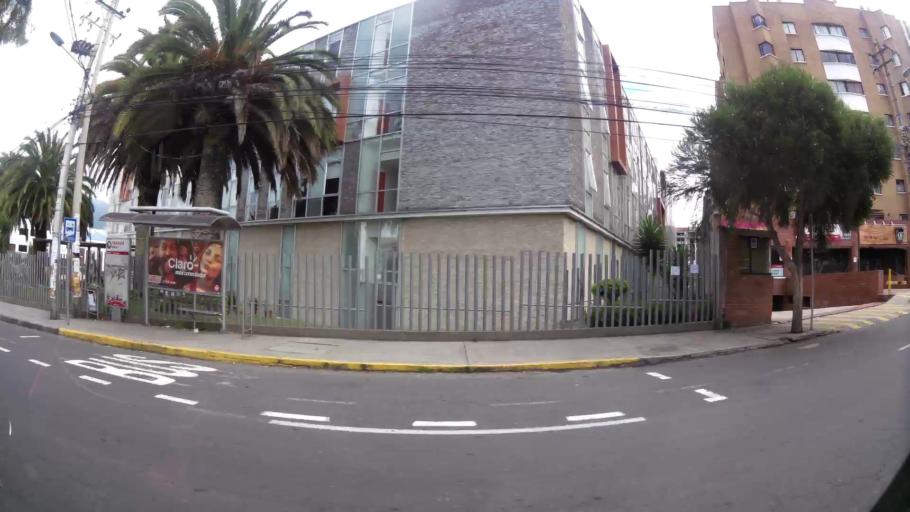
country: EC
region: Pichincha
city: Quito
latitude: -0.1683
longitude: -78.4725
